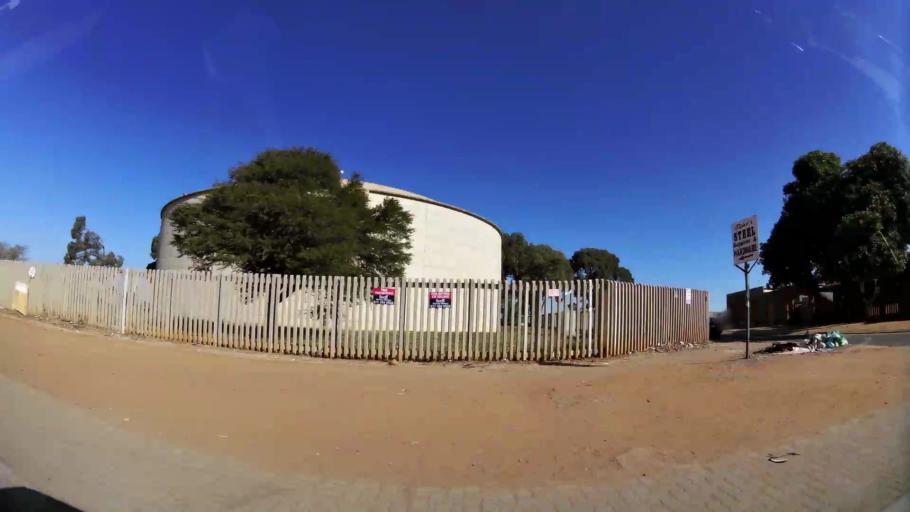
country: ZA
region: Gauteng
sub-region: Ekurhuleni Metropolitan Municipality
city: Tembisa
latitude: -26.0205
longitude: 28.2272
